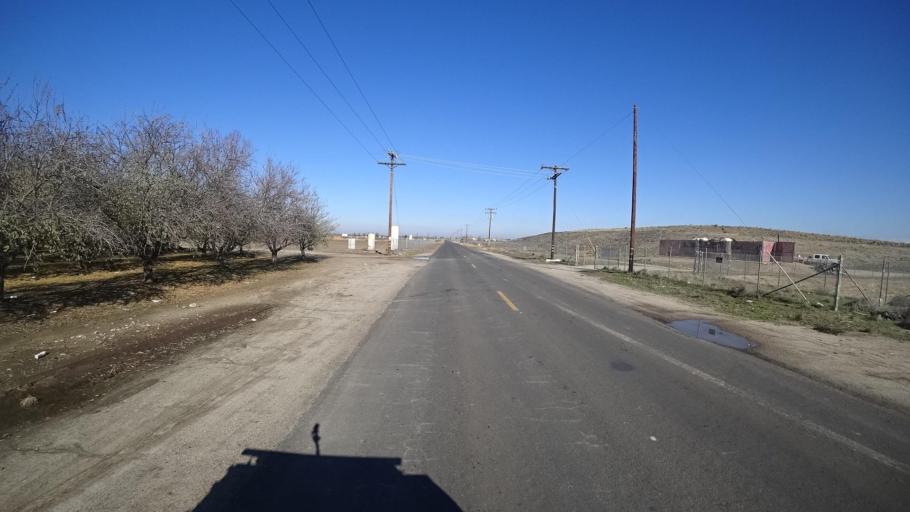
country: US
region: California
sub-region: Kern County
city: Delano
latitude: 35.7394
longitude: -119.2584
